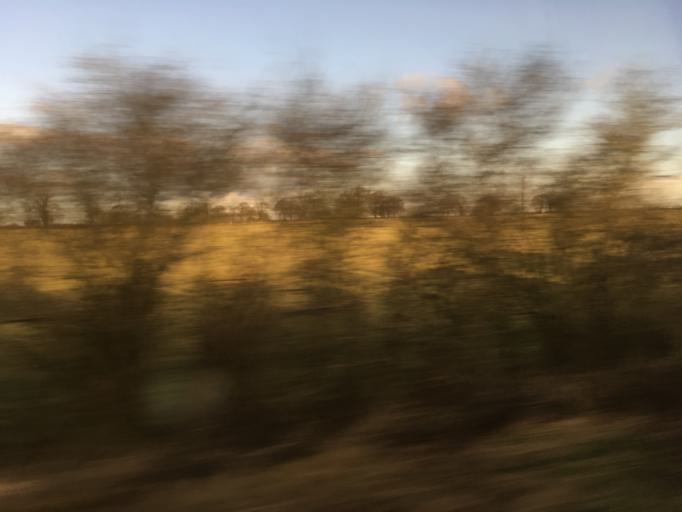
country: GB
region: England
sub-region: Wiltshire
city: Luckington
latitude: 51.5335
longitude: -2.2511
